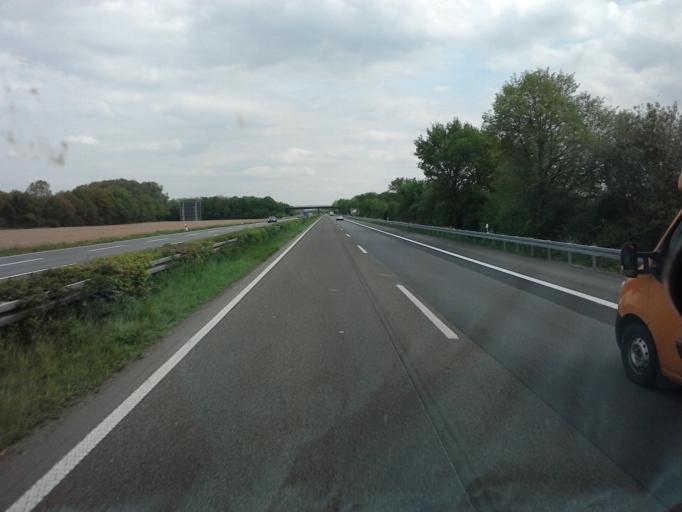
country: DE
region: North Rhine-Westphalia
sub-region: Regierungsbezirk Dusseldorf
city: Goch
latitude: 51.6697
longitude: 6.1235
